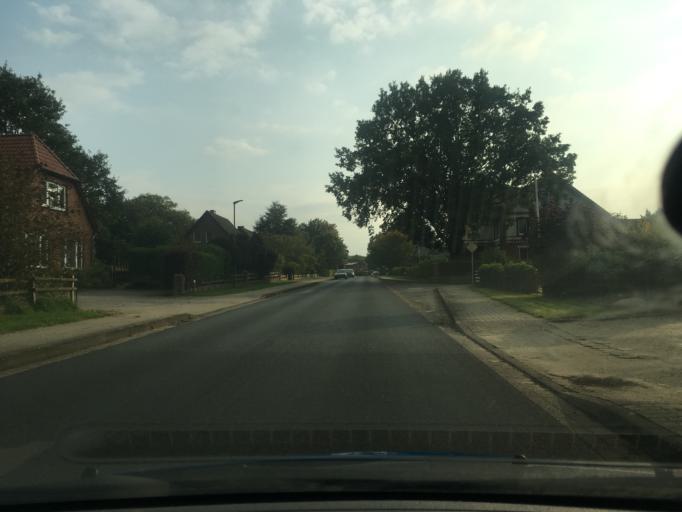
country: DE
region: Lower Saxony
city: Eyendorf
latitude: 53.2080
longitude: 10.1604
